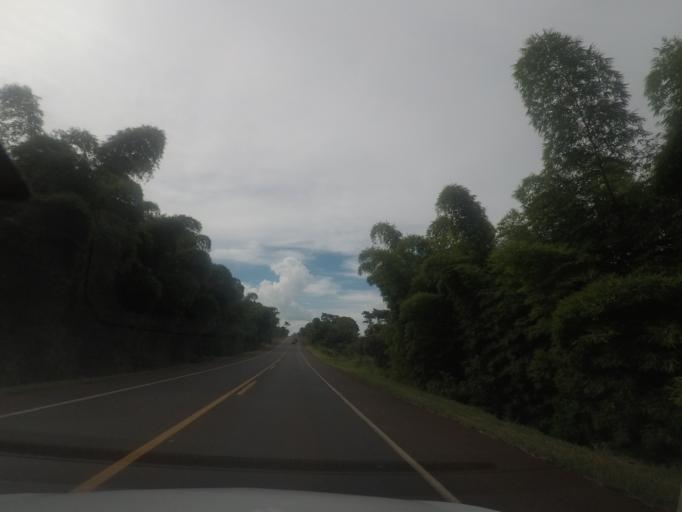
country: BR
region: Minas Gerais
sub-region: Prata
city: Prata
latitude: -19.2565
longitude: -48.9246
